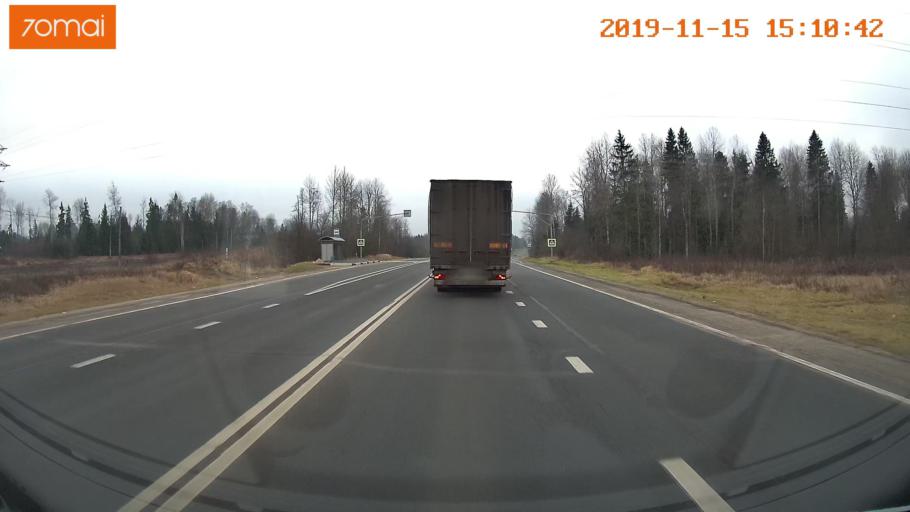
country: RU
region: Jaroslavl
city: Prechistoye
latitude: 58.3450
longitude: 40.2514
